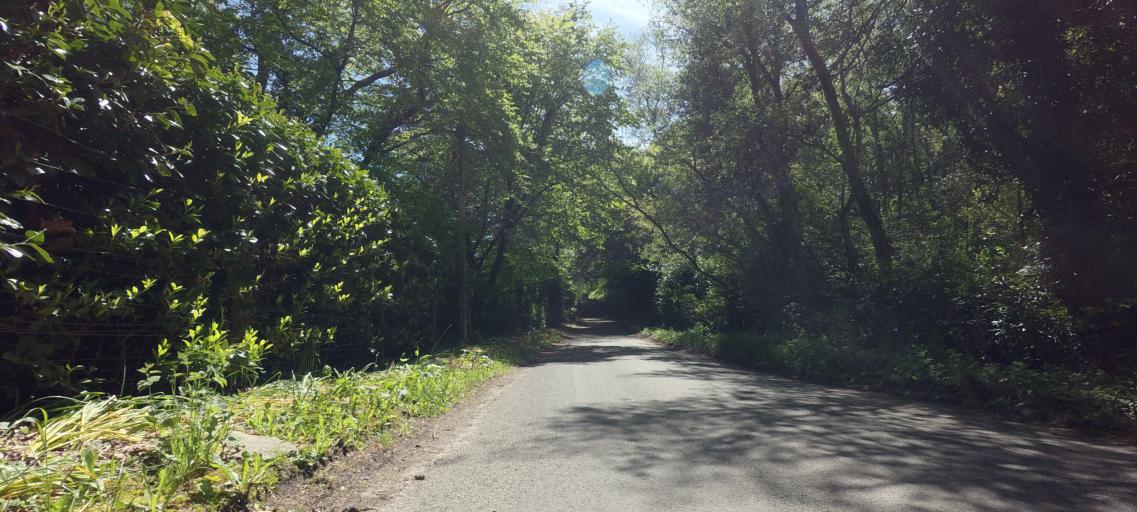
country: GB
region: England
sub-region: Dorset
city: Bovington Camp
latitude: 50.6885
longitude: -2.3179
